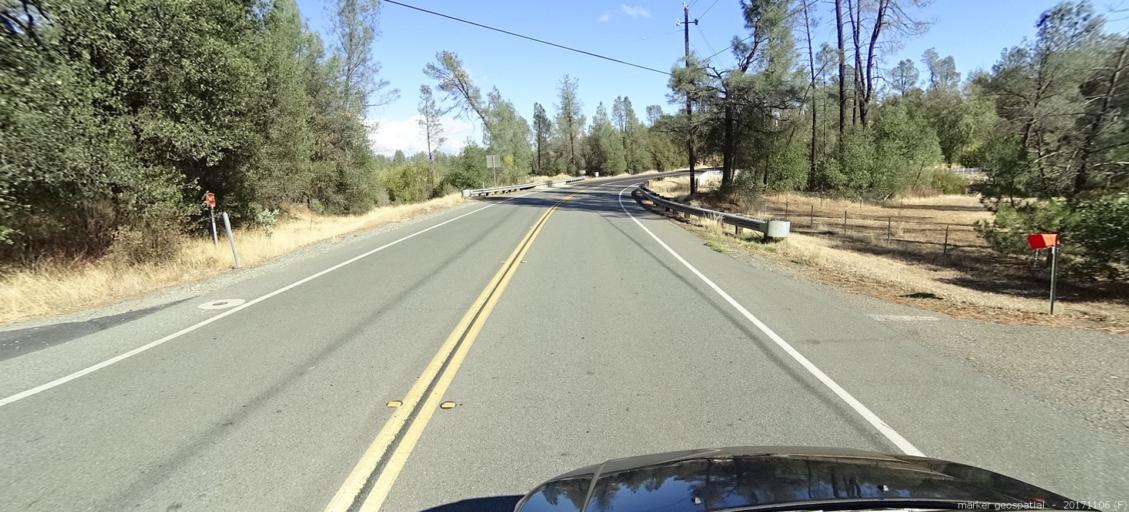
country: US
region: California
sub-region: Shasta County
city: Palo Cedro
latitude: 40.5918
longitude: -122.2958
